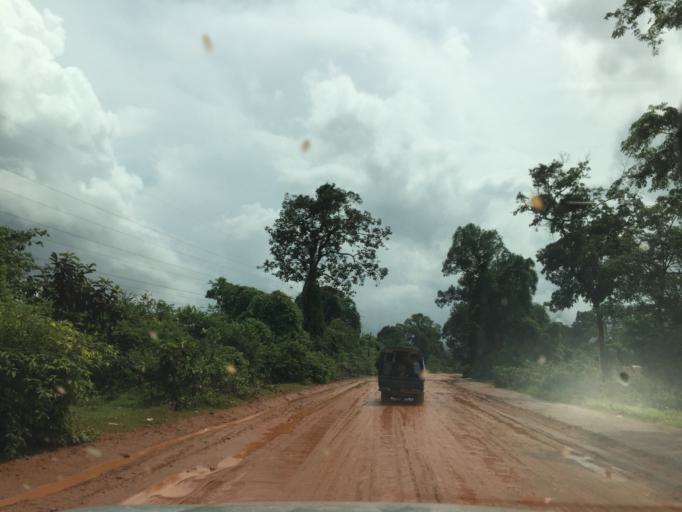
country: LA
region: Attapu
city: Attapu
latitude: 14.8102
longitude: 106.7786
